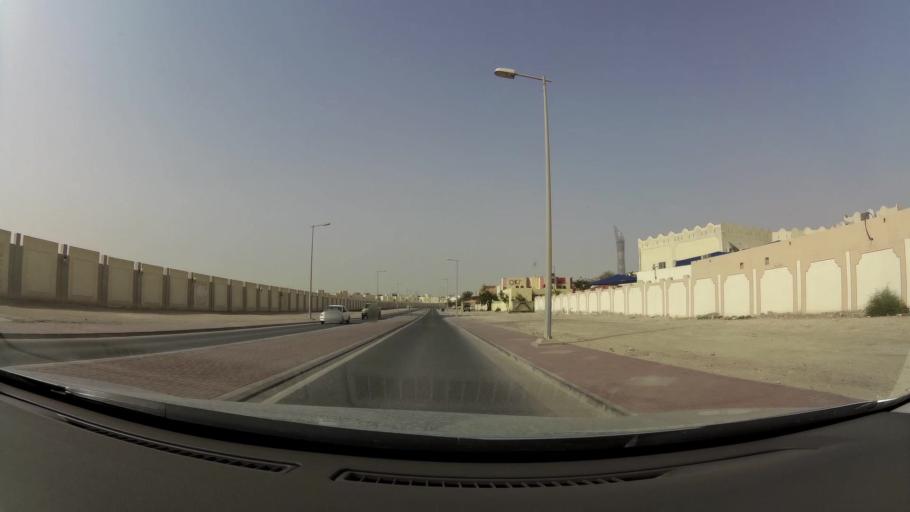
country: QA
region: Baladiyat ar Rayyan
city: Ar Rayyan
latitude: 25.2486
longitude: 51.4379
